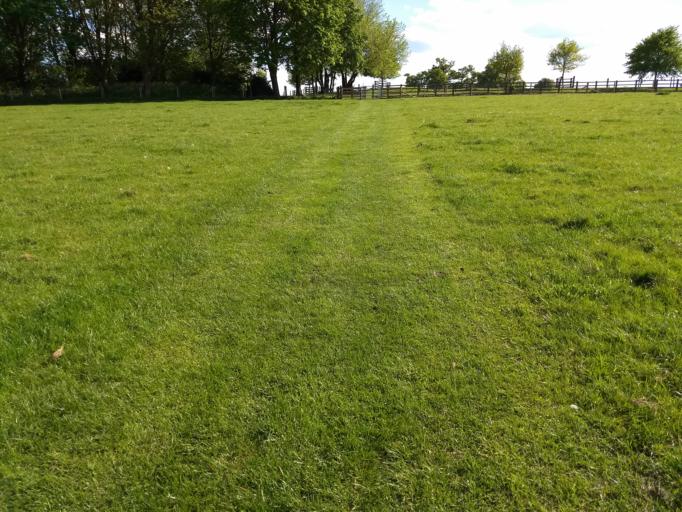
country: GB
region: England
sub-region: Milton Keynes
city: Castlethorpe
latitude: 52.0688
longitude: -0.8209
